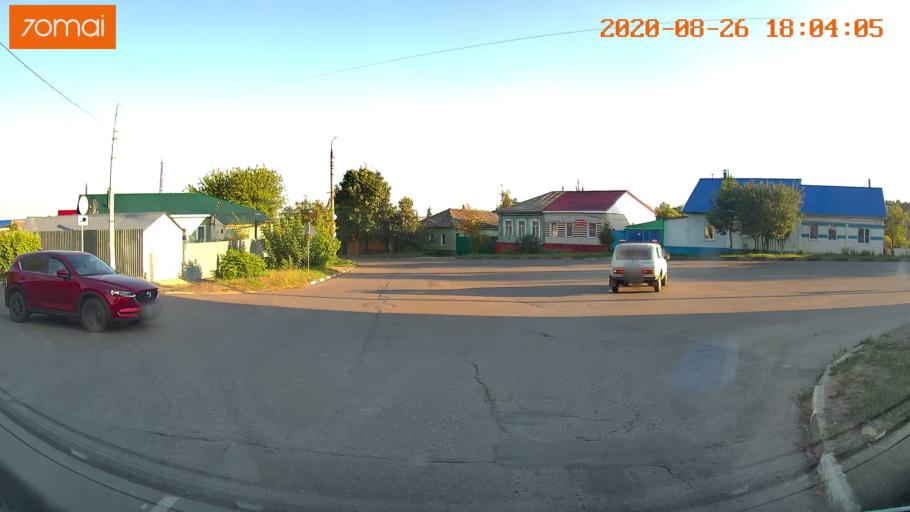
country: RU
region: Tula
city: Yefremov
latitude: 53.1388
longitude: 38.1144
